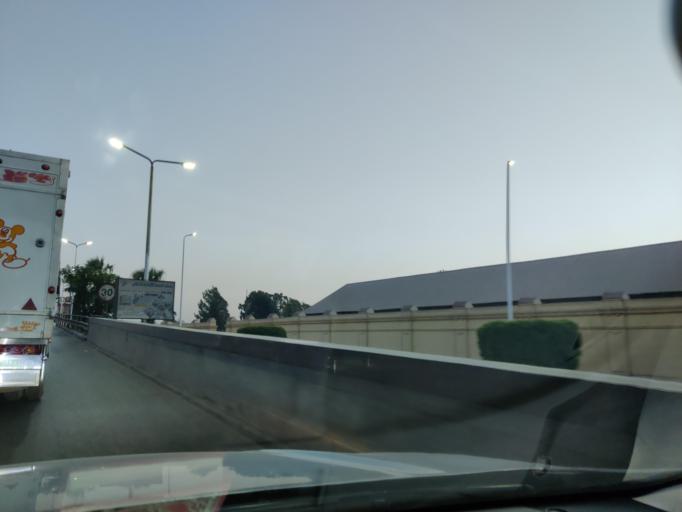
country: EG
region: Muhafazat al Qahirah
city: Cairo
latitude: 30.1011
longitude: 31.3057
